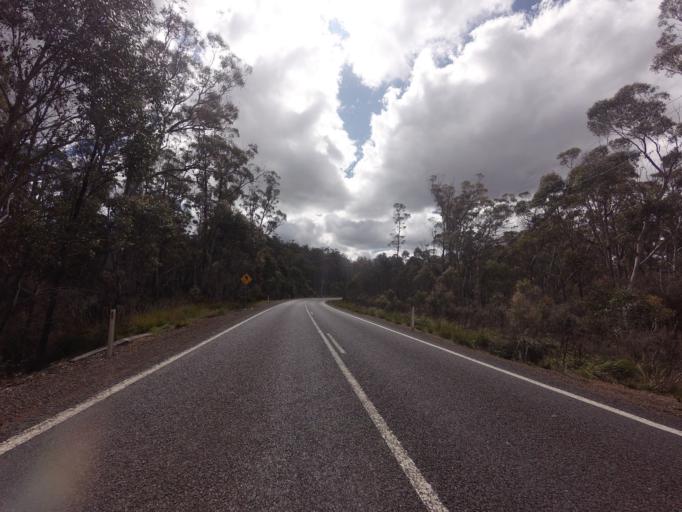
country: AU
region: Tasmania
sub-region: Northern Midlands
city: Evandale
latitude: -42.0166
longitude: 147.7358
